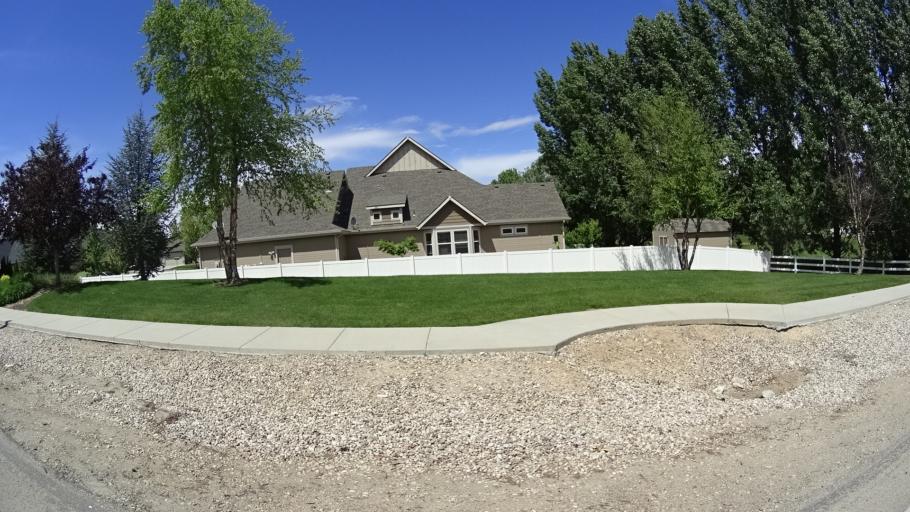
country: US
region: Idaho
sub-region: Ada County
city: Meridian
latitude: 43.5757
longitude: -116.3829
